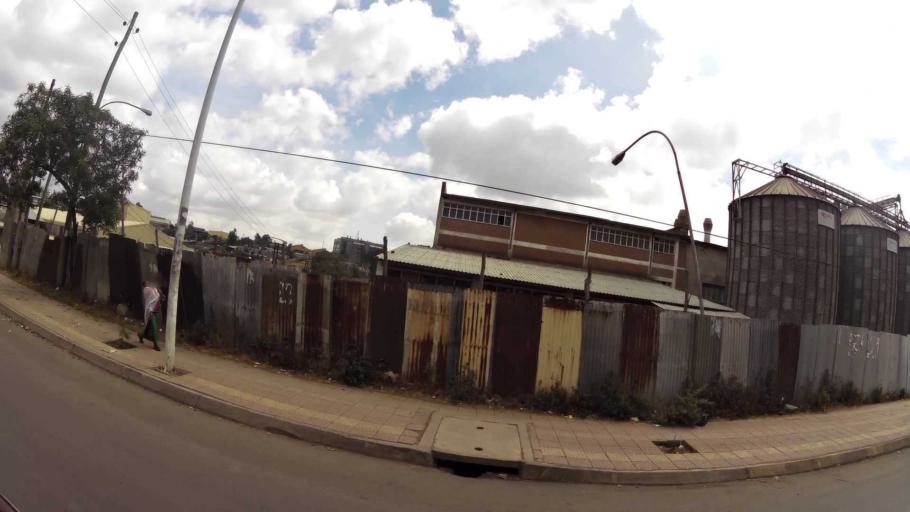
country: ET
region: Adis Abeba
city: Addis Ababa
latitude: 8.9467
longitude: 38.7583
